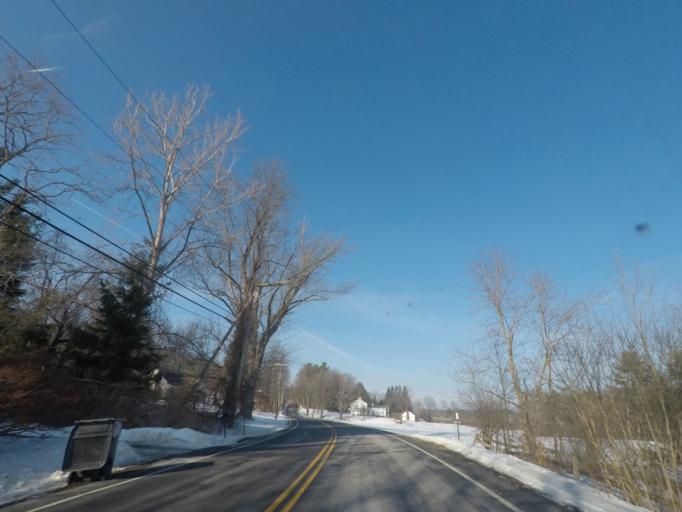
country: US
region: Massachusetts
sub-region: Berkshire County
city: Richmond
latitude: 42.4760
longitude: -73.3903
